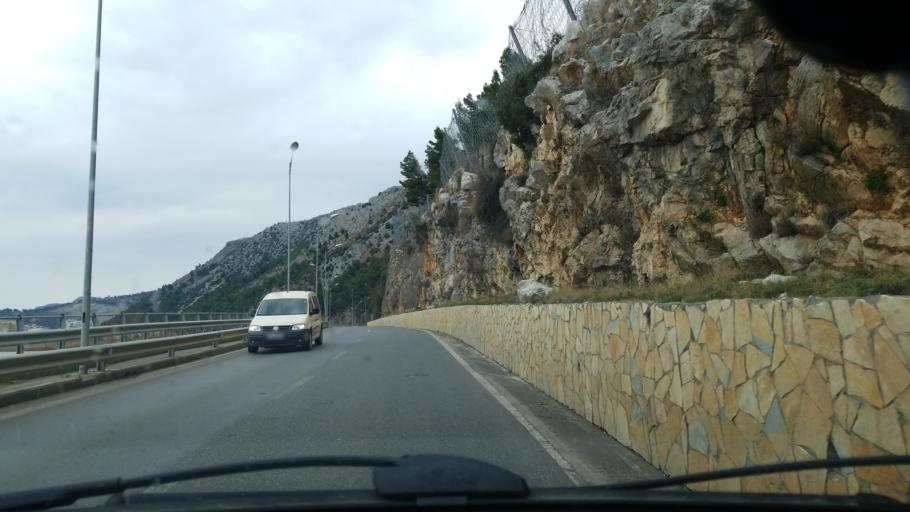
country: AL
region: Lezhe
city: Shengjin
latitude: 41.8020
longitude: 19.6157
